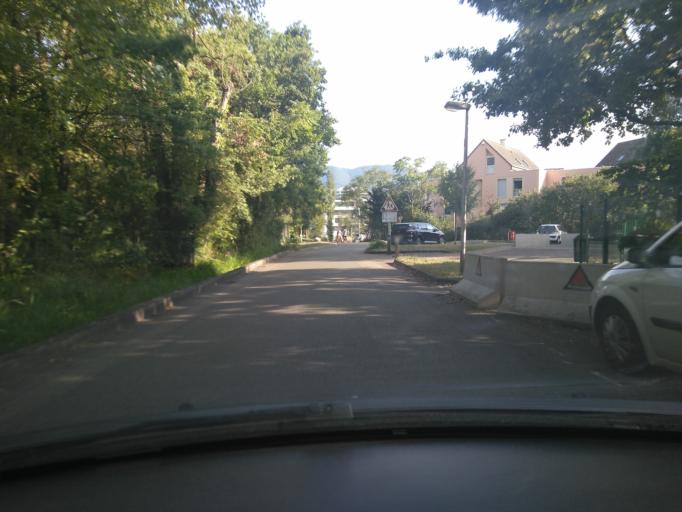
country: FR
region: Rhone-Alpes
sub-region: Departement de l'Isere
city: Meylan
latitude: 45.2125
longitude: 5.7865
